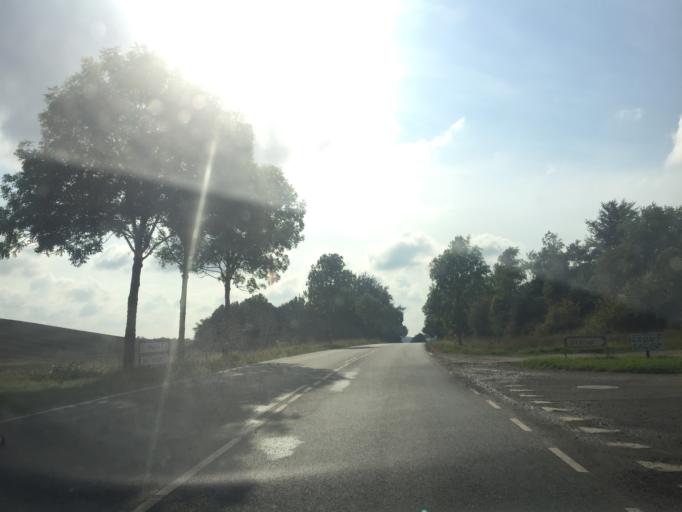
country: DK
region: Zealand
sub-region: Holbaek Kommune
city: Tollose
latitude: 55.6462
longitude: 11.8068
